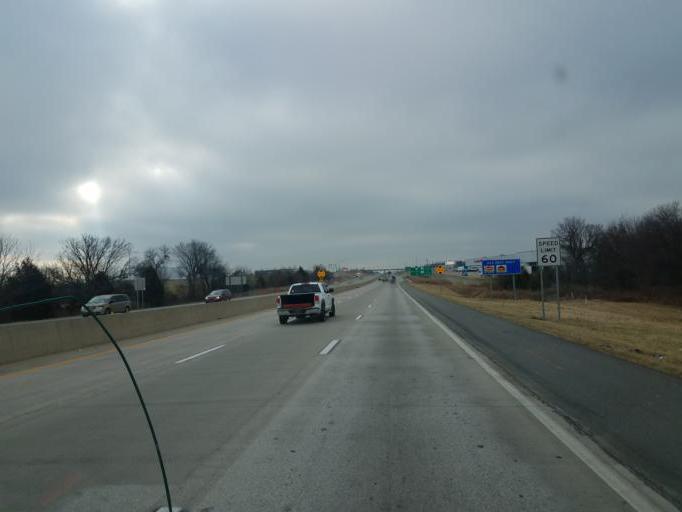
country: US
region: Missouri
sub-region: Greene County
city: Springfield
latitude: 37.2311
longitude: -93.2252
